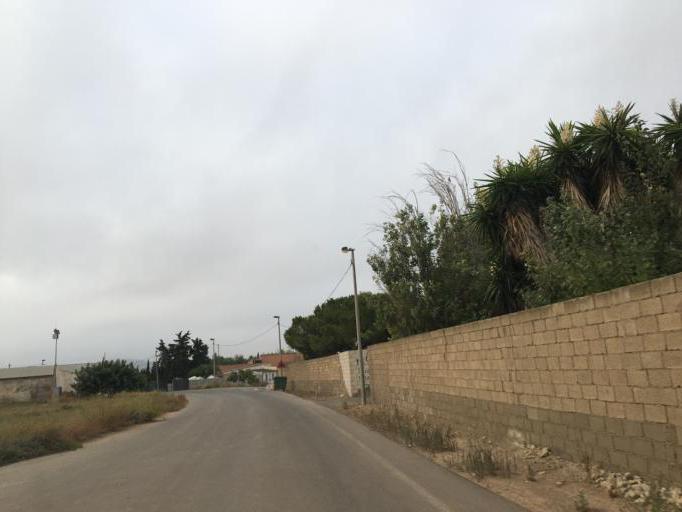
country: ES
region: Murcia
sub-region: Murcia
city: Cartagena
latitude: 37.6657
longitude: -0.9525
